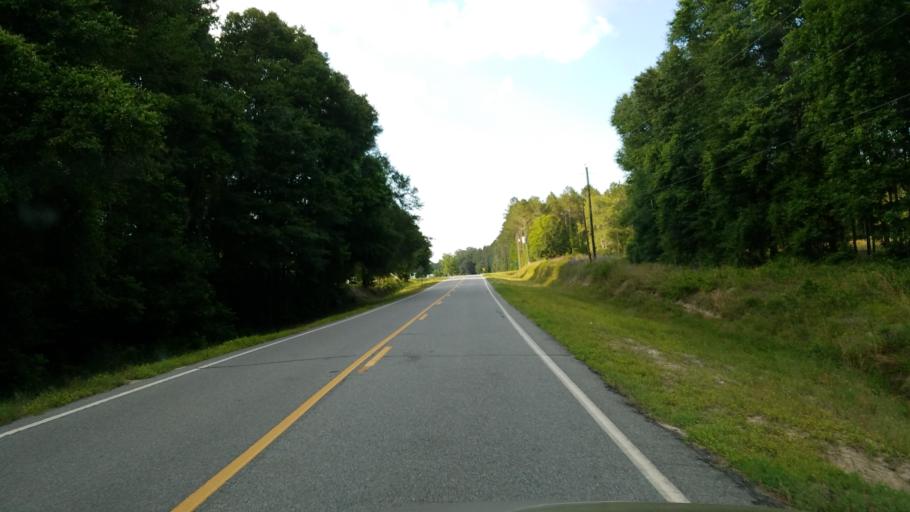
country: US
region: Georgia
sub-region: Echols County
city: Statenville
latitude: 30.7861
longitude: -83.0547
